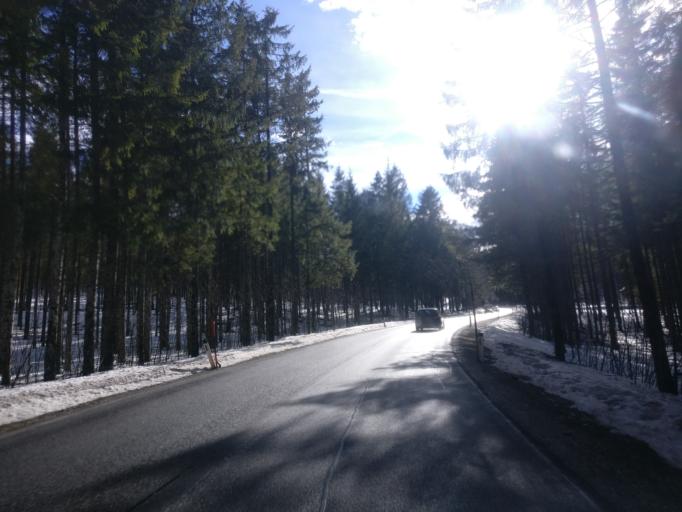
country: AT
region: Styria
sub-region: Politischer Bezirk Liezen
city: Sankt Gallen
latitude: 47.6255
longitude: 14.5556
